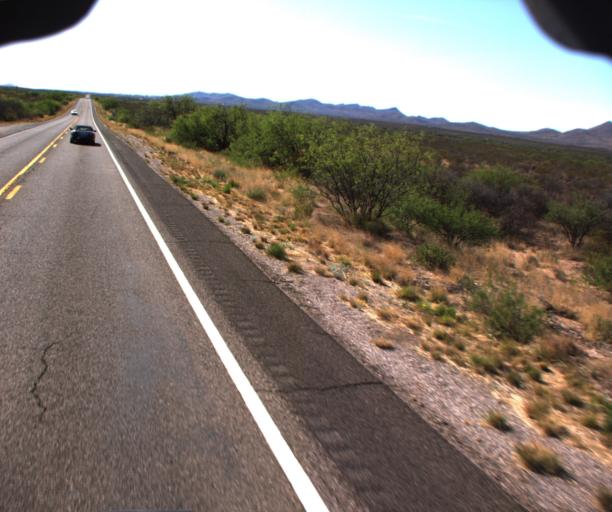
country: US
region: Arizona
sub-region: Cochise County
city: Tombstone
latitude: 31.7664
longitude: -110.1192
